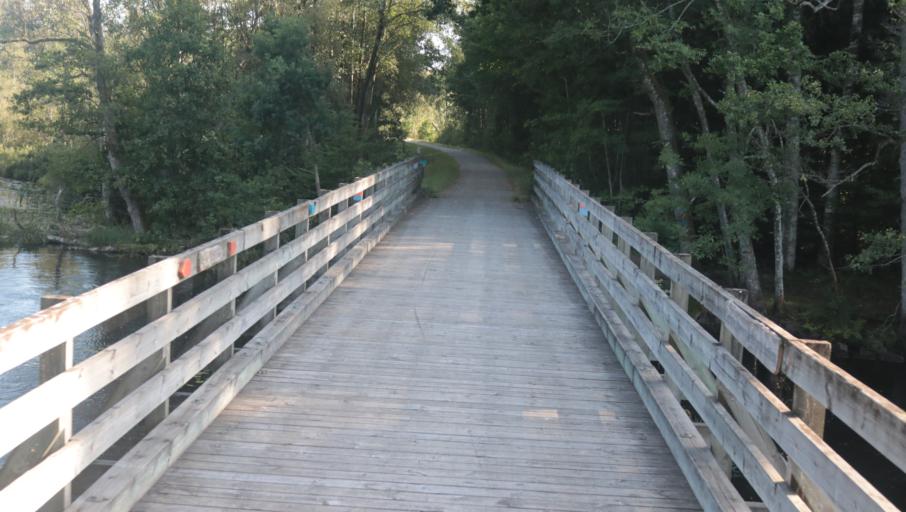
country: SE
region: Blekinge
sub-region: Karlshamns Kommun
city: Svangsta
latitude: 56.3770
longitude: 14.6802
